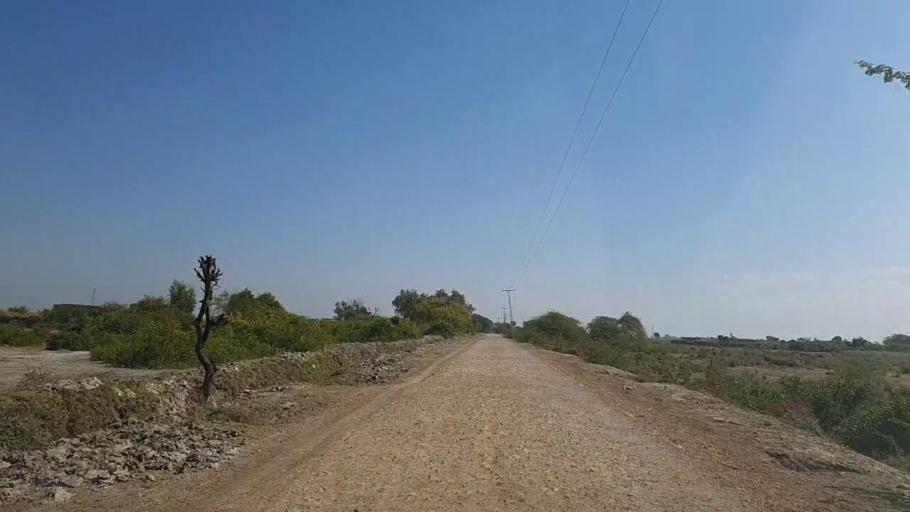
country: PK
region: Sindh
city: Pithoro
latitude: 25.4195
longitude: 69.3901
